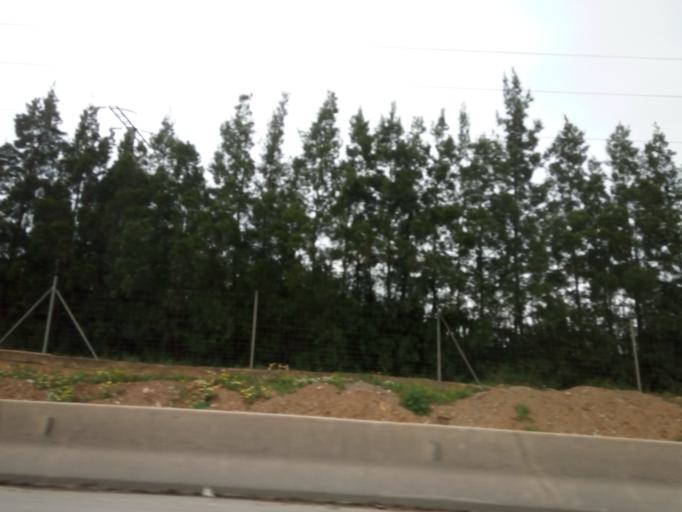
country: DZ
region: Blida
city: Chiffa
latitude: 36.4721
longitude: 2.7731
